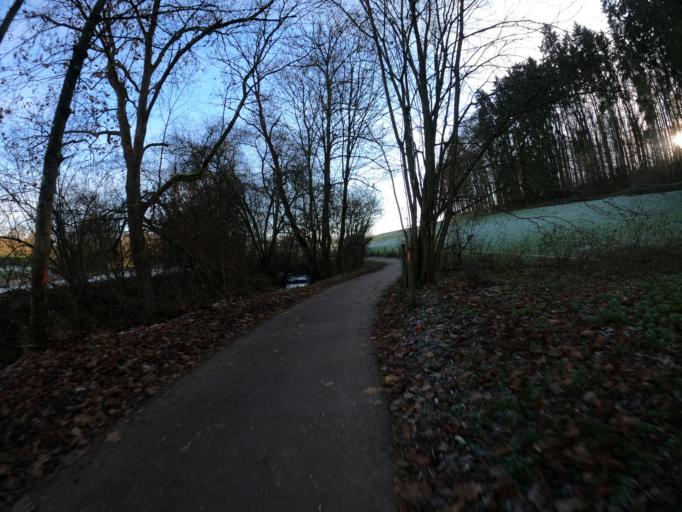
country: DE
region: Baden-Wuerttemberg
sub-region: Regierungsbezirk Stuttgart
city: Goeppingen
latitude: 48.6933
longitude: 9.6204
